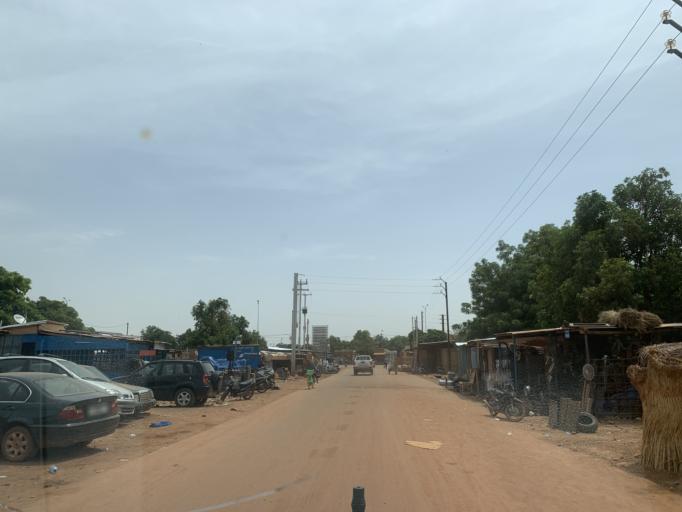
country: BF
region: Centre
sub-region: Kadiogo Province
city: Ouagadougou
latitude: 12.3385
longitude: -1.5147
